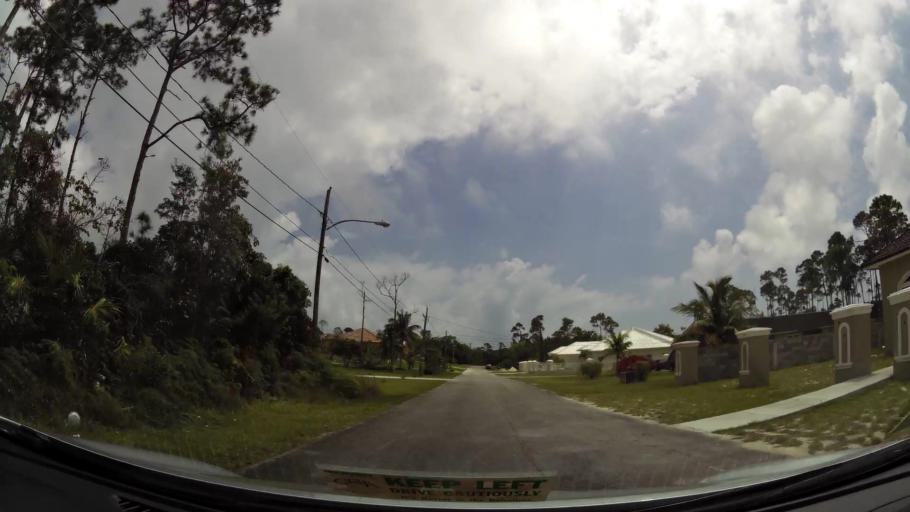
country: BS
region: Freeport
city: Lucaya
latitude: 26.5231
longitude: -78.6509
